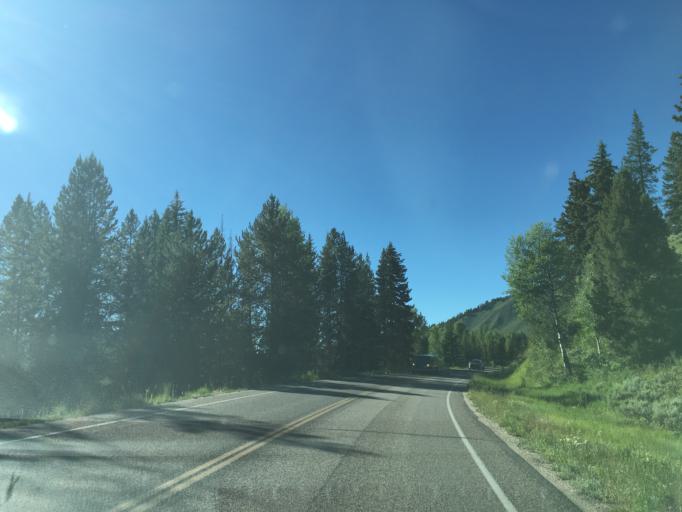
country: US
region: Wyoming
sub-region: Teton County
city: Jackson
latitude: 43.8463
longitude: -110.5167
